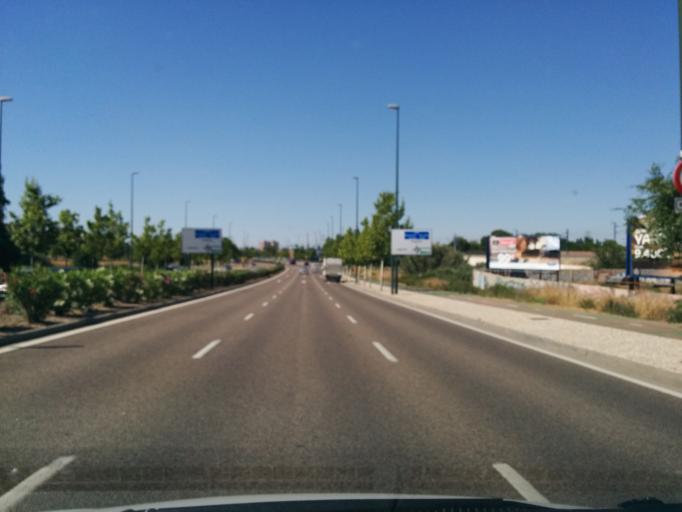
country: ES
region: Aragon
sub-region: Provincia de Zaragoza
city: Zaragoza
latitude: 41.6547
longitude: -0.8536
